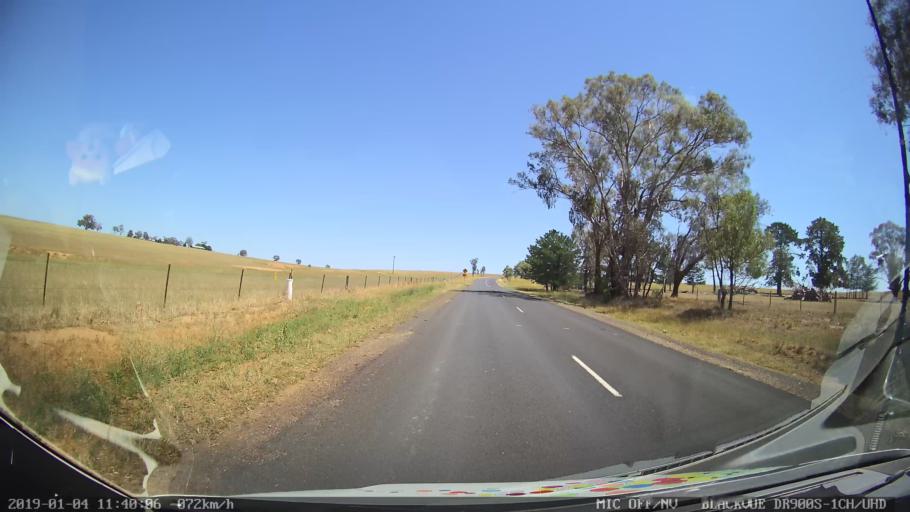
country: AU
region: New South Wales
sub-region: Cabonne
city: Molong
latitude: -33.0076
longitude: 148.7895
